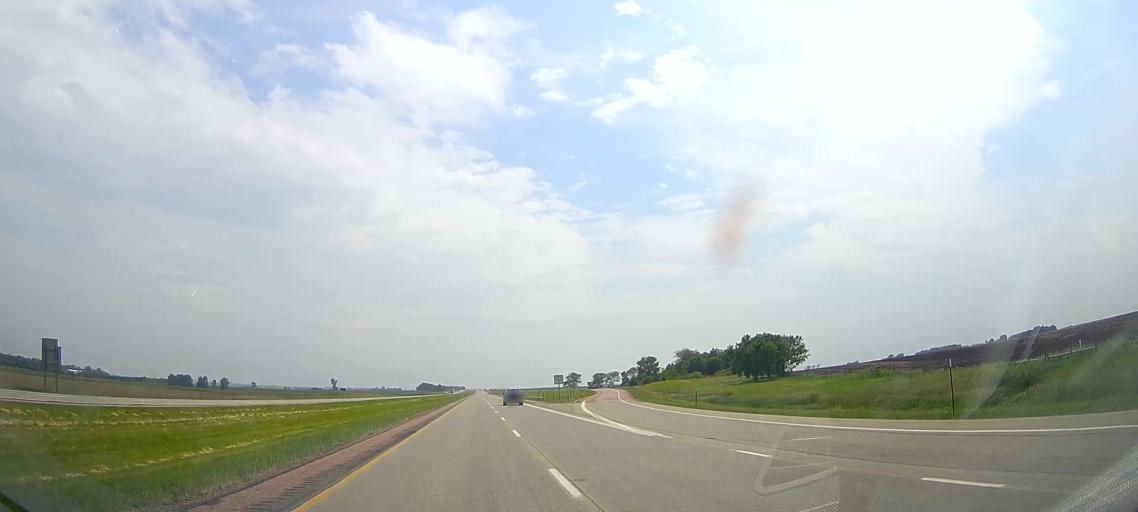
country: US
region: South Dakota
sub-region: Union County
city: Beresford
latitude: 42.9919
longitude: -96.7956
